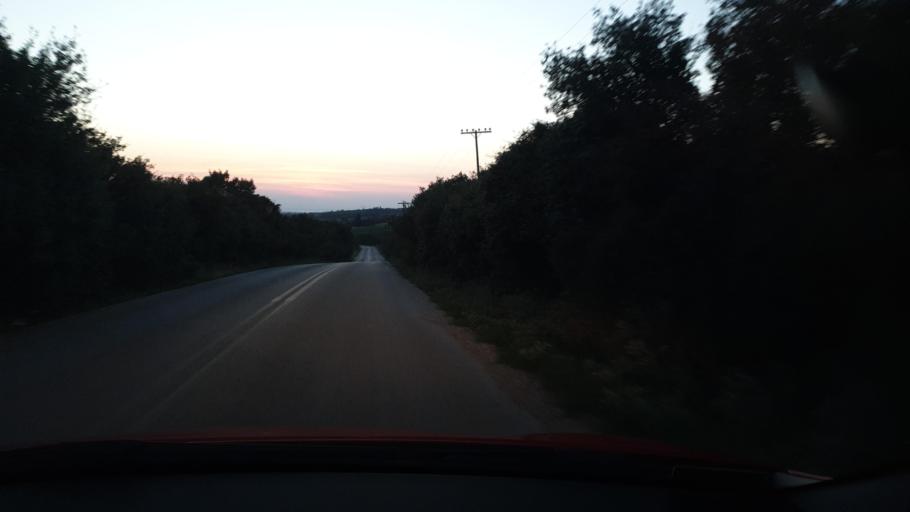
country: GR
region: Central Macedonia
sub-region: Nomos Thessalonikis
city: Vasilika
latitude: 40.5085
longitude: 23.1438
